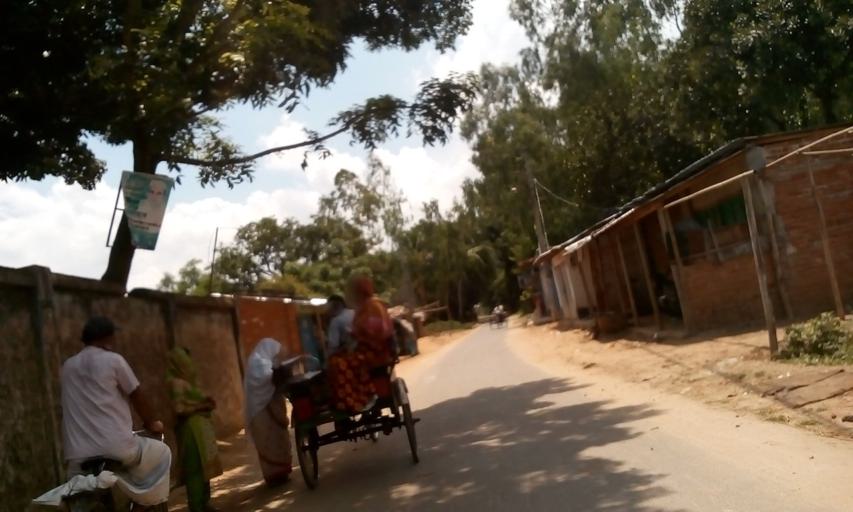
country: IN
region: West Bengal
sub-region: Dakshin Dinajpur
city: Balurghat
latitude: 25.3782
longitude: 88.9928
